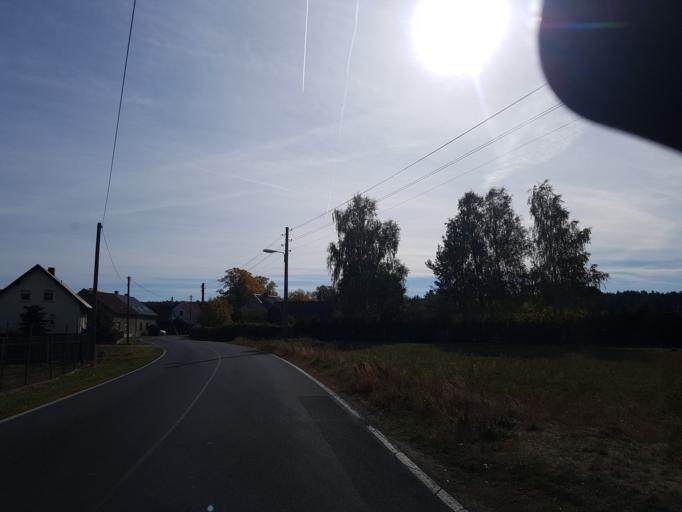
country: DE
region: Brandenburg
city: Schlieben
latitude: 51.7587
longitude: 13.3530
